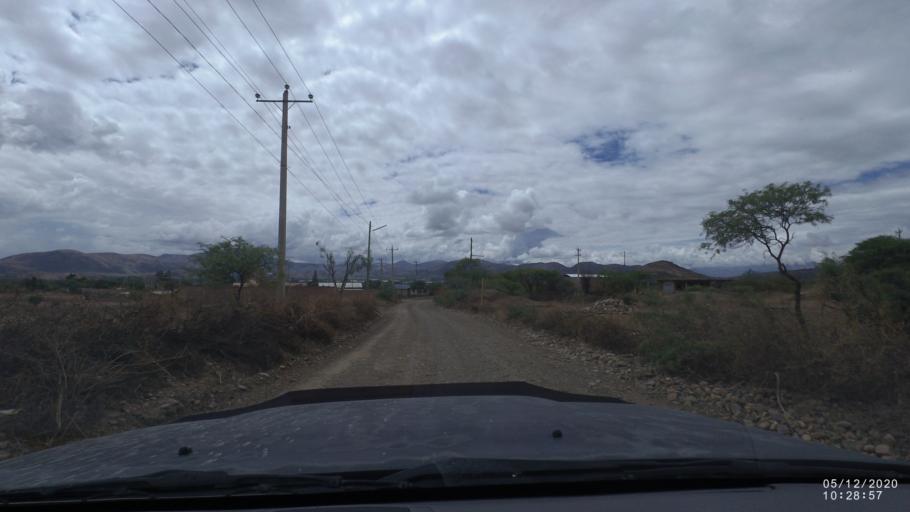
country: BO
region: Cochabamba
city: Sipe Sipe
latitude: -17.5406
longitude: -66.2699
